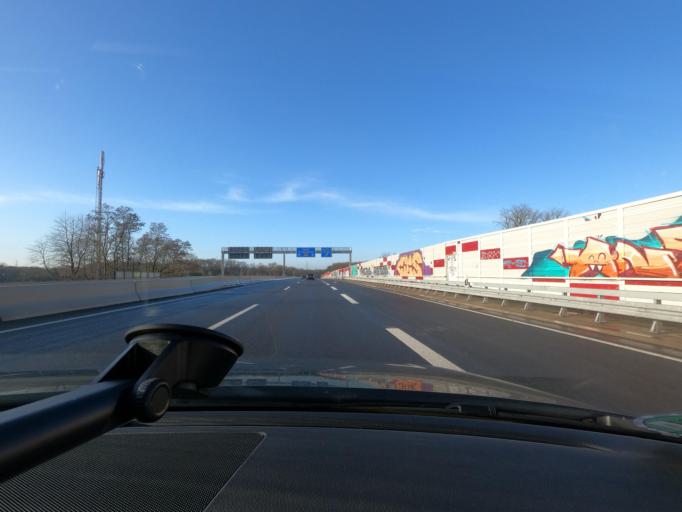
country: DE
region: North Rhine-Westphalia
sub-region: Regierungsbezirk Dusseldorf
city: Hochfeld
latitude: 51.3525
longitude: 6.7458
